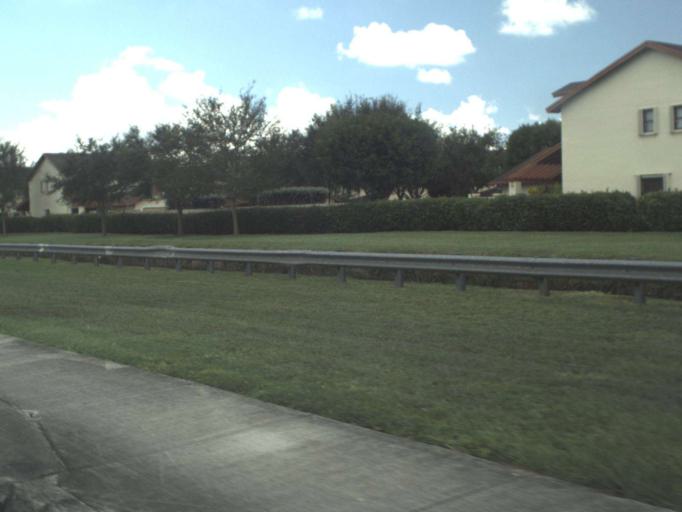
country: US
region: Florida
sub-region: Miami-Dade County
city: The Crossings
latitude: 25.6747
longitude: -80.4166
